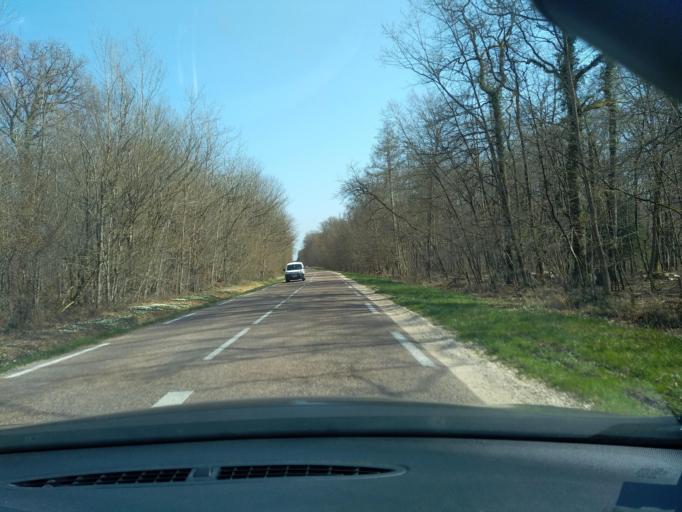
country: FR
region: Franche-Comte
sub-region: Departement du Jura
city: Mont-sous-Vaudrey
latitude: 46.9613
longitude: 5.5465
